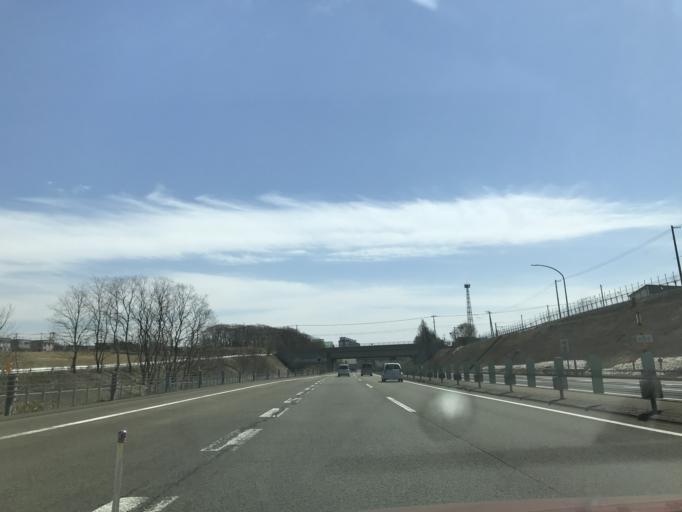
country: JP
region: Hokkaido
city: Ebetsu
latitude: 43.0929
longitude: 141.5001
